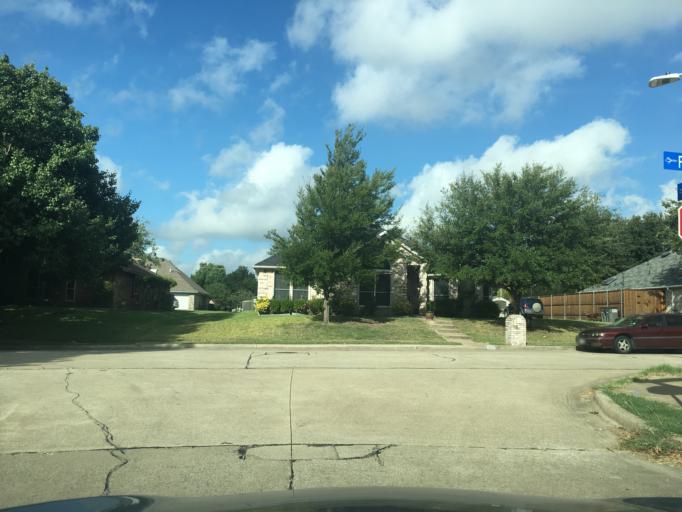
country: US
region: Texas
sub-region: Dallas County
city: Sachse
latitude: 32.9688
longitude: -96.5904
